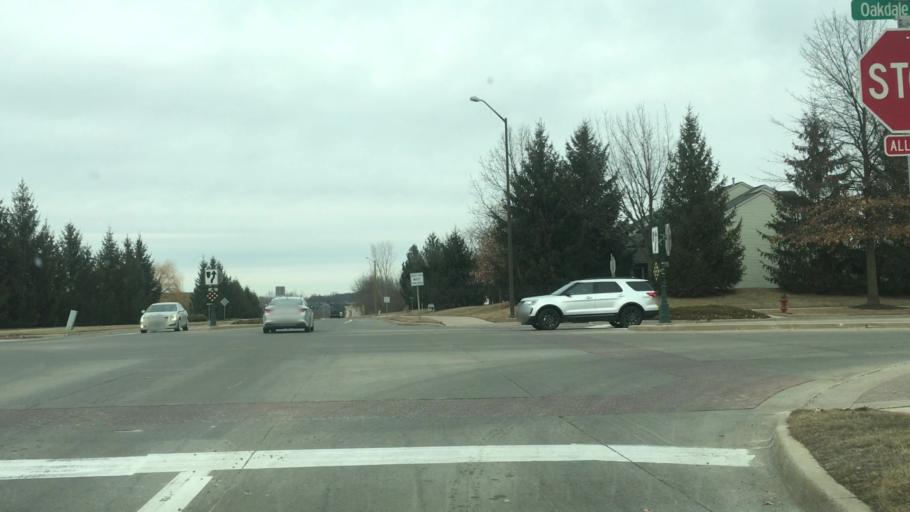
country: US
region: Iowa
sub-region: Johnson County
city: Coralville
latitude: 41.7042
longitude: -91.5878
